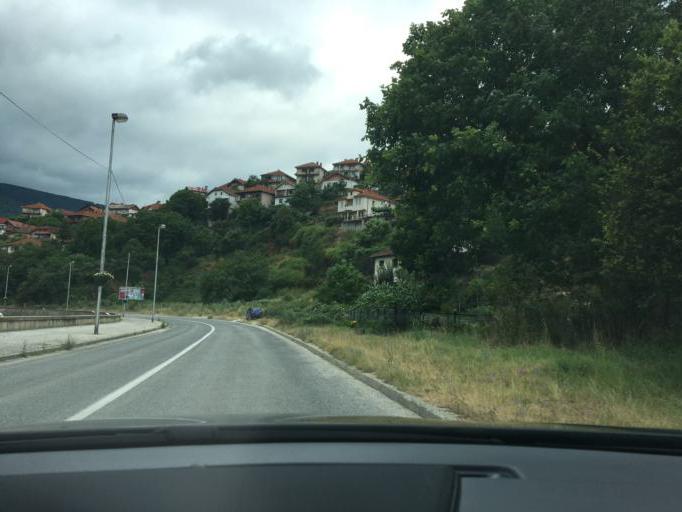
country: MK
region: Kriva Palanka
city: Kriva Palanka
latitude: 42.2057
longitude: 22.3336
